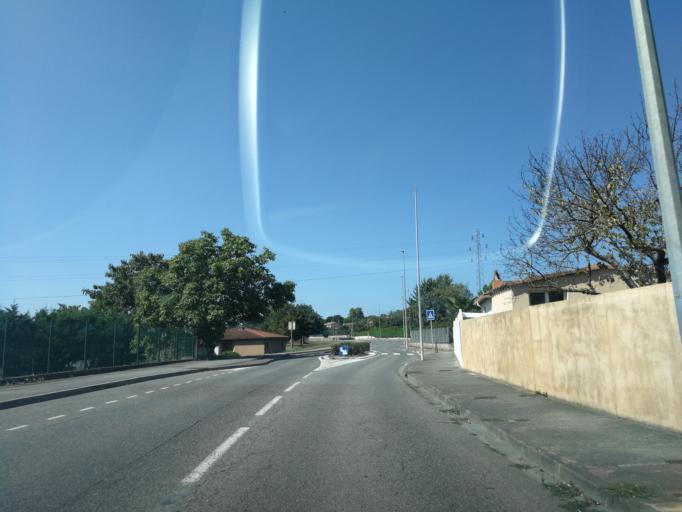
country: FR
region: Midi-Pyrenees
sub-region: Departement de la Haute-Garonne
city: Saint-Orens-de-Gameville
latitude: 43.5816
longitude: 1.5351
